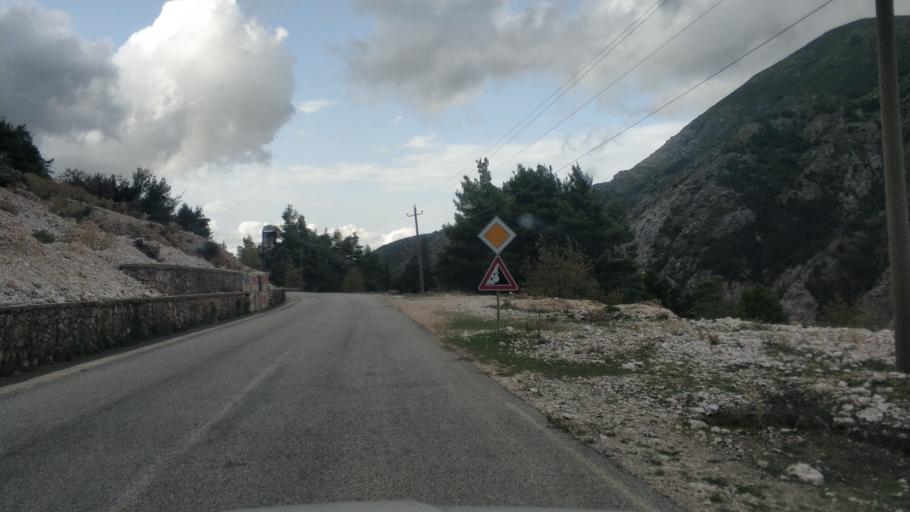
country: AL
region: Vlore
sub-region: Rrethi i Vlores
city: Orikum
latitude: 40.2479
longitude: 19.5453
